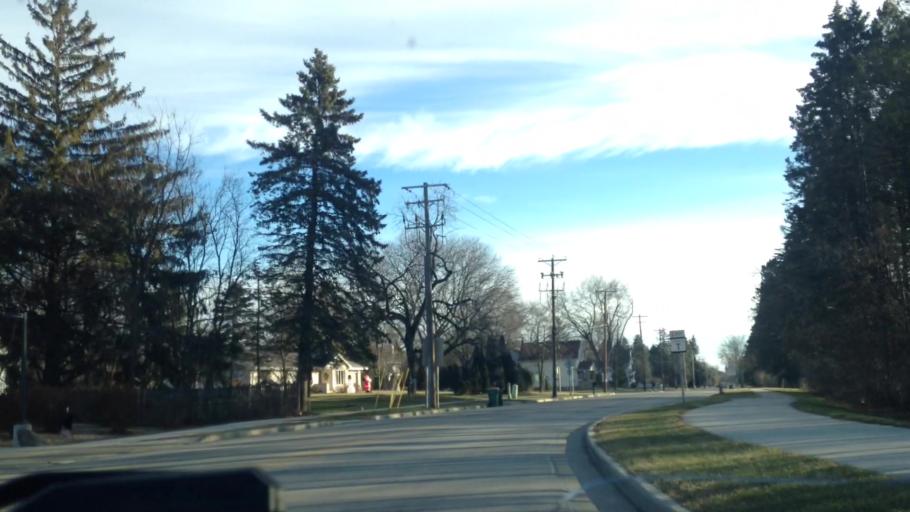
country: US
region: Wisconsin
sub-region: Ozaukee County
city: Cedarburg
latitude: 43.2935
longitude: -88.0039
